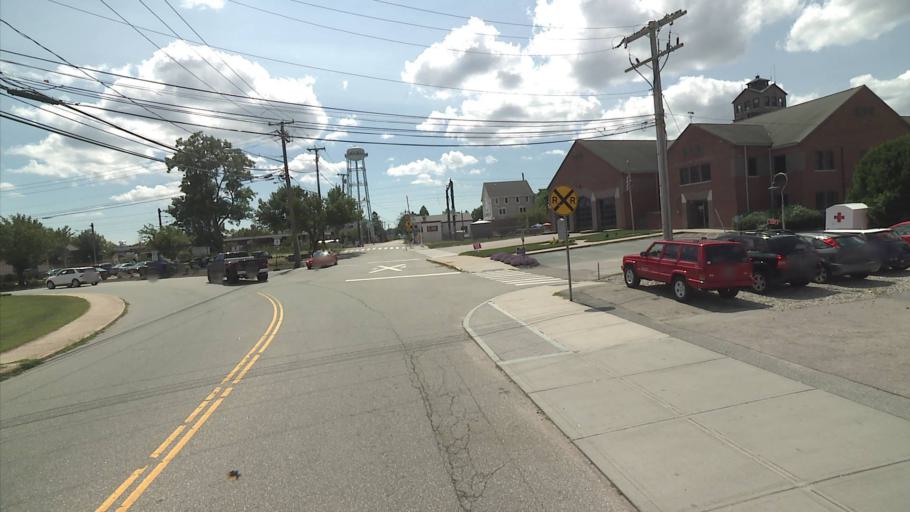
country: US
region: Connecticut
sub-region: New London County
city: Mystic
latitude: 41.3516
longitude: -71.9639
